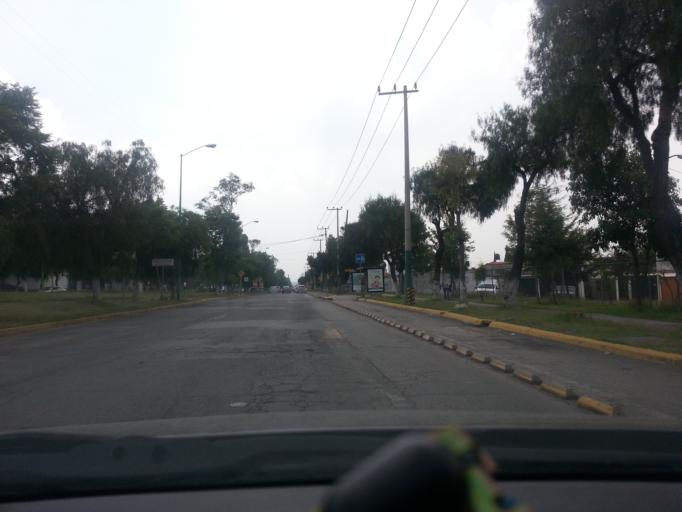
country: MX
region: Mexico
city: Cuautitlan Izcalli
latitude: 19.6574
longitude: -99.2118
